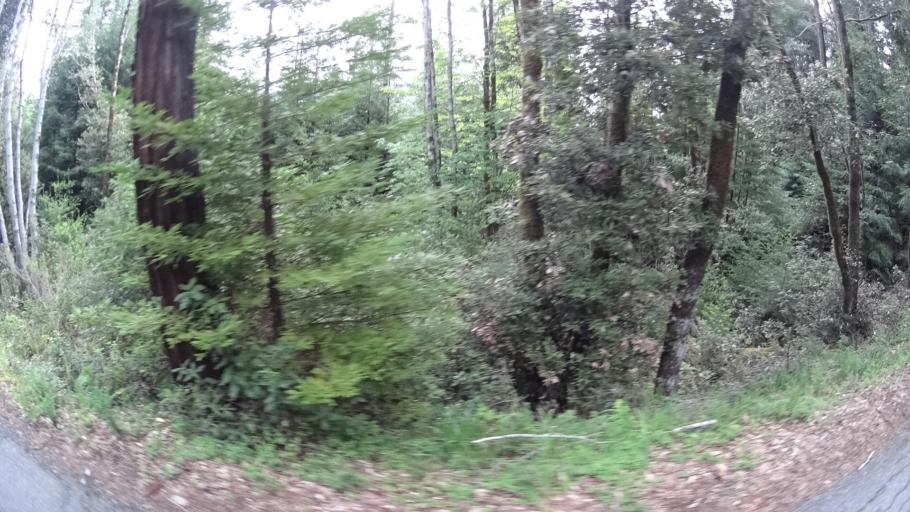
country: US
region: California
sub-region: Humboldt County
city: Redway
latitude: 40.3384
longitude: -123.9125
